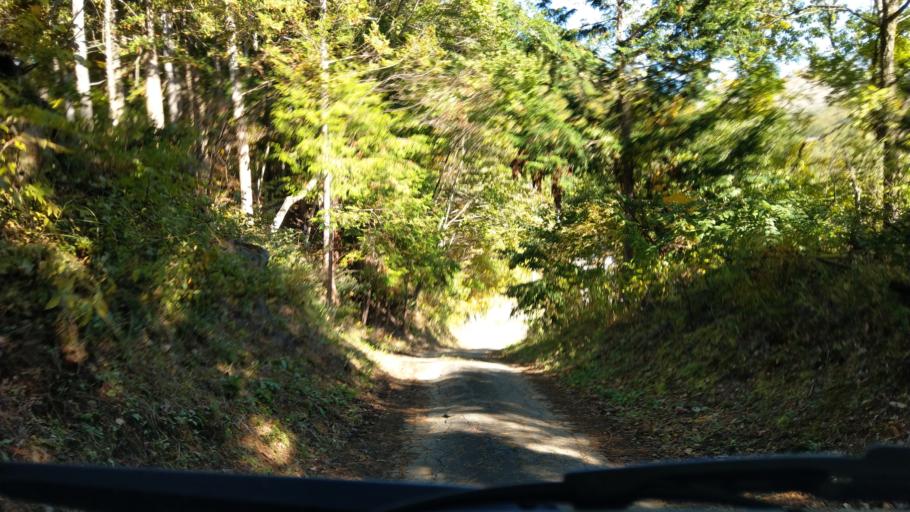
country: JP
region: Nagano
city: Komoro
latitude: 36.3642
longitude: 138.4457
